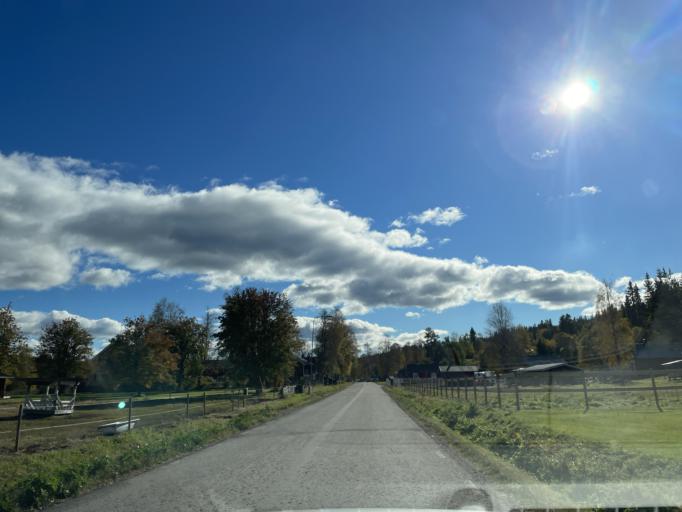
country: SE
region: Dalarna
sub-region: Malung-Saelens kommun
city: Malung
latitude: 61.1603
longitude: 13.2565
